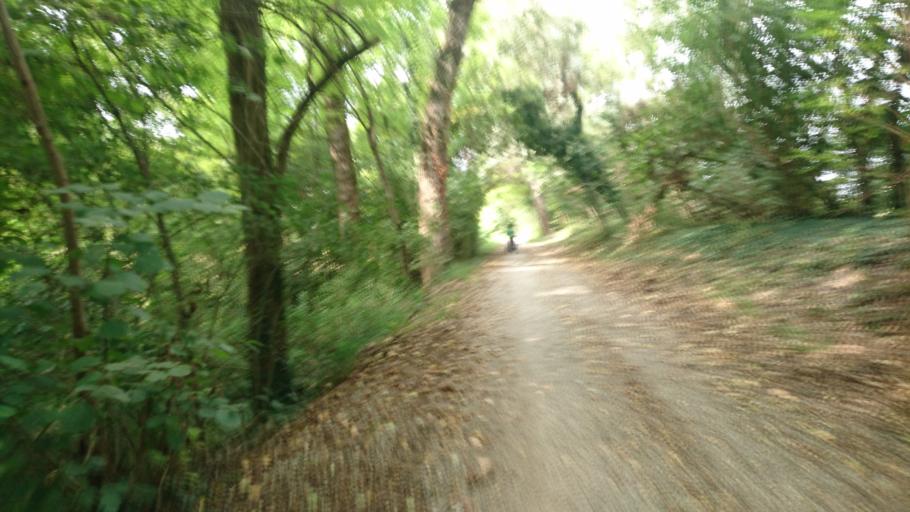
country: IT
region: Veneto
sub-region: Provincia di Padova
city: Piazzola sul Brenta
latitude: 45.5703
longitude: 11.7639
